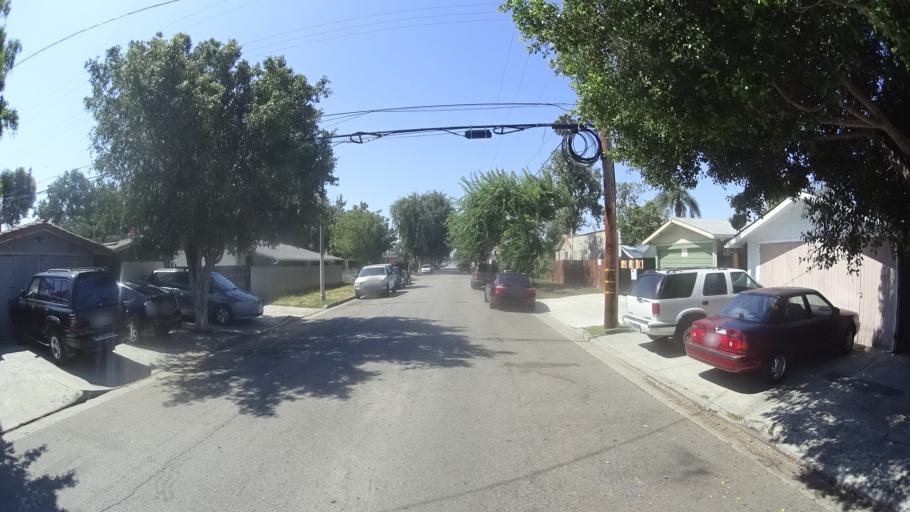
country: US
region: California
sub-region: Los Angeles County
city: Westmont
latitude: 33.9776
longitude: -118.3025
